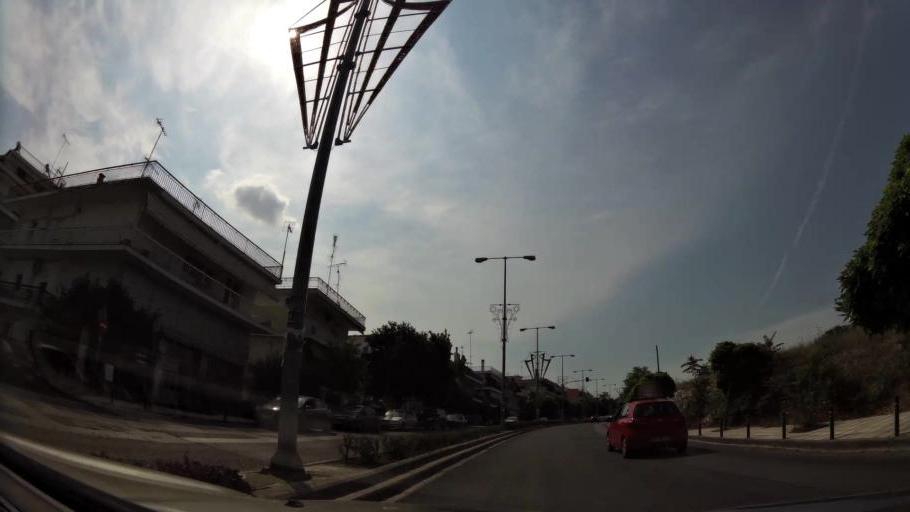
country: GR
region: Central Macedonia
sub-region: Nomos Thessalonikis
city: Agios Pavlos
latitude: 40.6466
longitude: 22.9621
